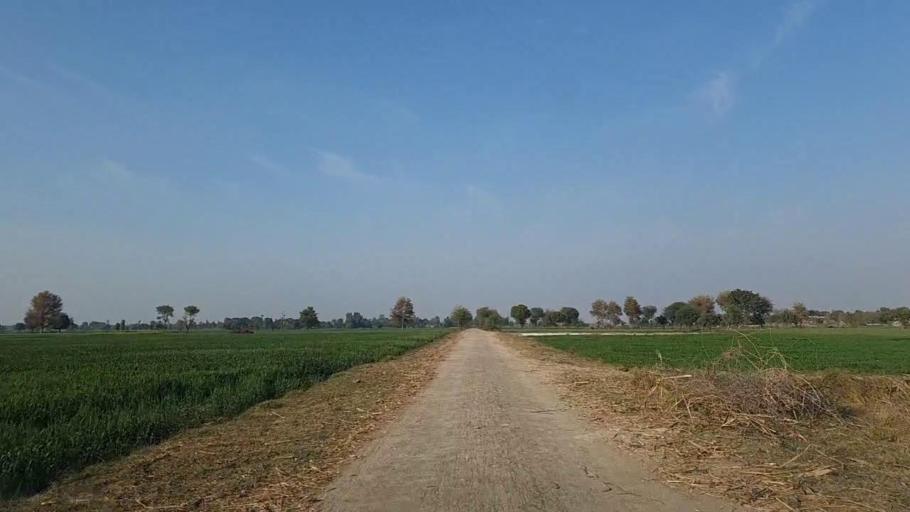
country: PK
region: Sindh
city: Nawabshah
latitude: 26.3750
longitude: 68.4849
